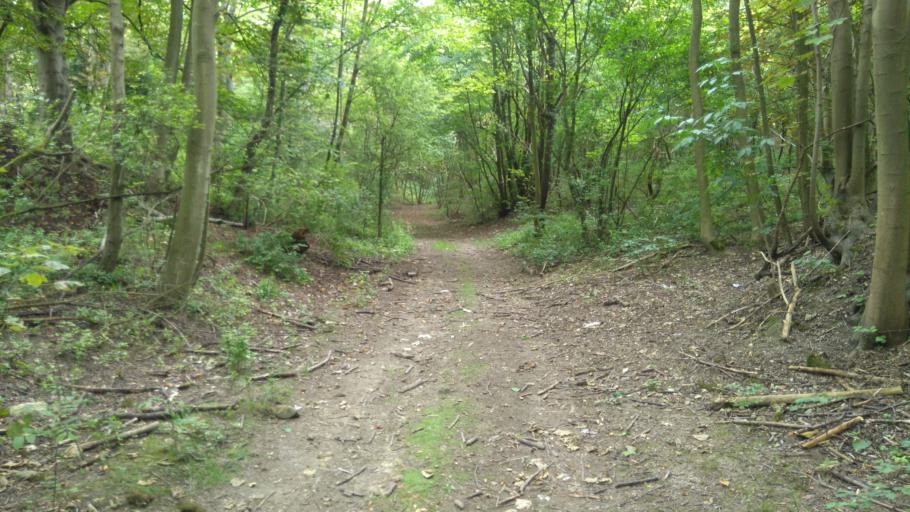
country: FR
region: Picardie
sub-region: Departement de l'Oise
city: Saint-Maximin
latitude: 49.2398
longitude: 2.4536
